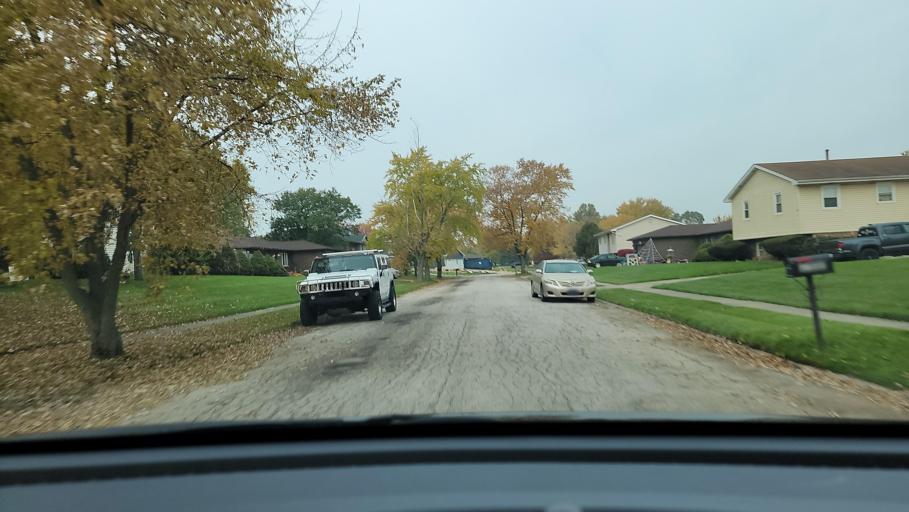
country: US
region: Indiana
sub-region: Porter County
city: Portage
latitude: 41.5594
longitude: -87.1713
